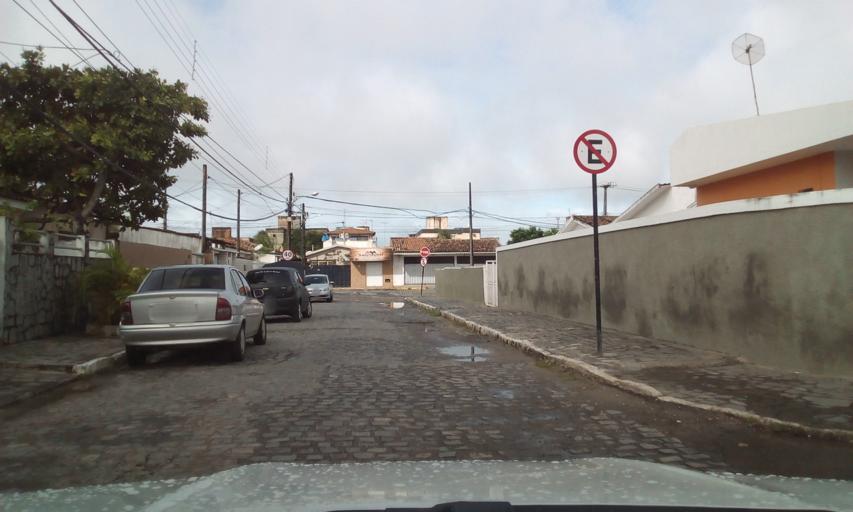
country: BR
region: Paraiba
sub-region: Joao Pessoa
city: Joao Pessoa
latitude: -7.1637
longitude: -34.8371
